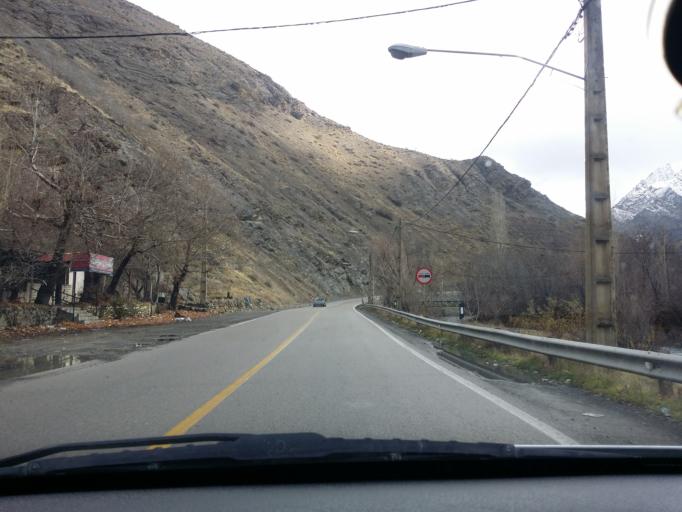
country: IR
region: Tehran
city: Tajrish
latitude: 36.0312
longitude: 51.2329
